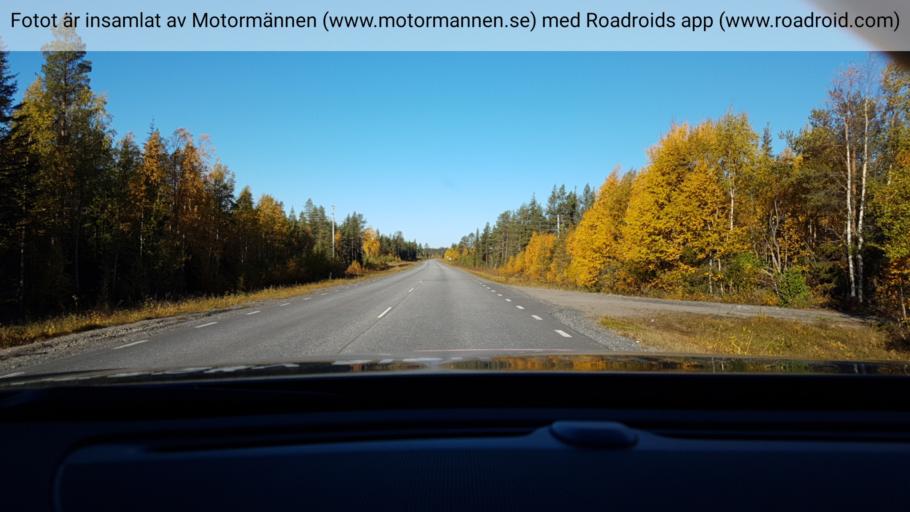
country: SE
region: Vaesterbotten
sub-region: Skelleftea Kommun
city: Storvik
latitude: 65.3727
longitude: 20.3824
